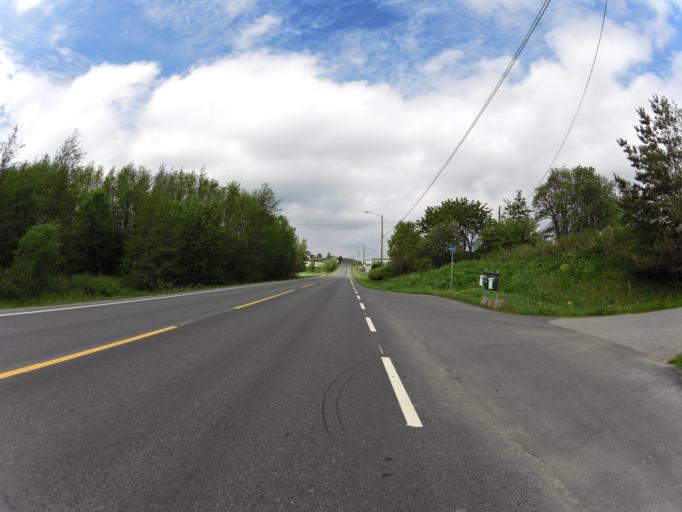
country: NO
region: Ostfold
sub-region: Rade
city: Karlshus
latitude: 59.3394
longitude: 10.9340
